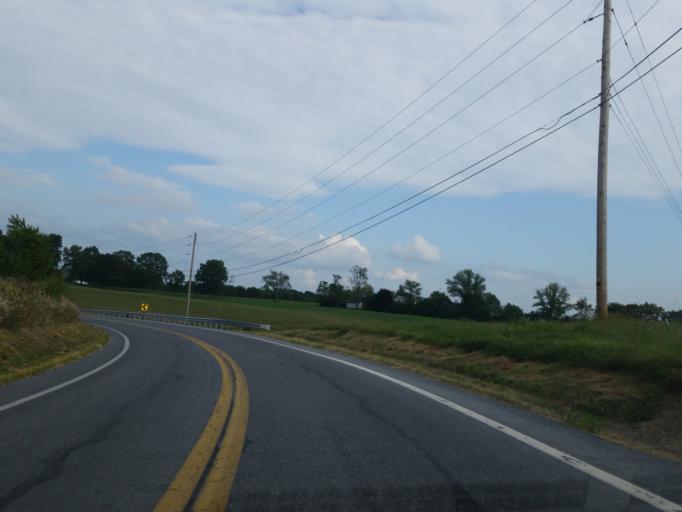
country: US
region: Pennsylvania
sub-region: Lebanon County
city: Jonestown
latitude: 40.3997
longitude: -76.5281
